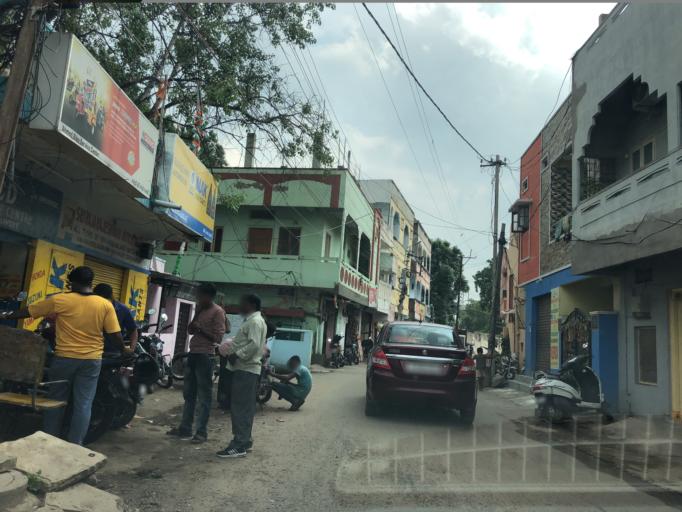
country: IN
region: Telangana
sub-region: Hyderabad
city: Malkajgiri
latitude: 17.4456
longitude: 78.4780
